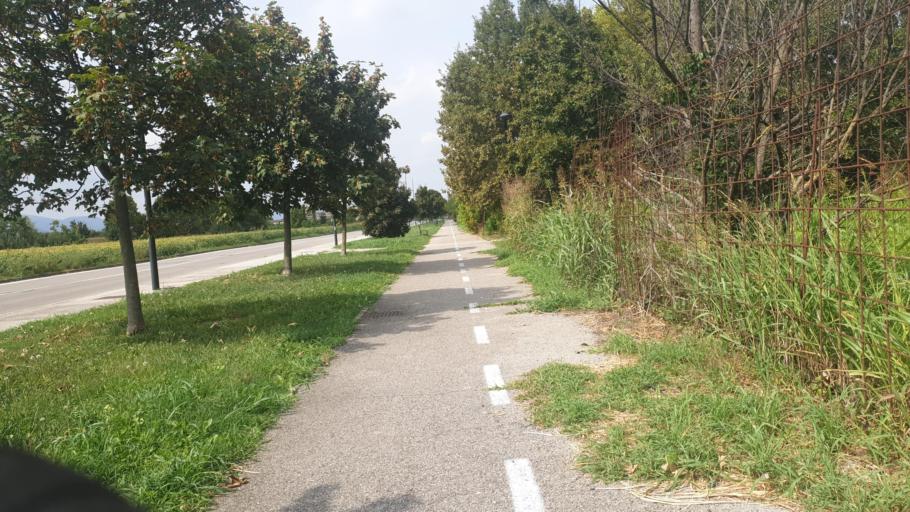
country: IT
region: Veneto
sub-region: Provincia di Padova
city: Albignasego
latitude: 45.3370
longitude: 11.8788
